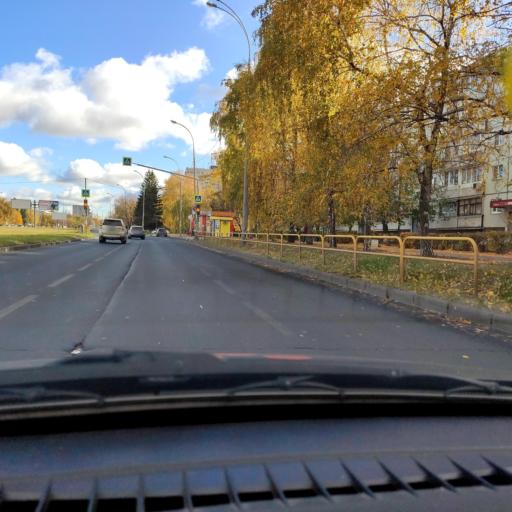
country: RU
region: Samara
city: Tol'yatti
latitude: 53.5284
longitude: 49.2836
